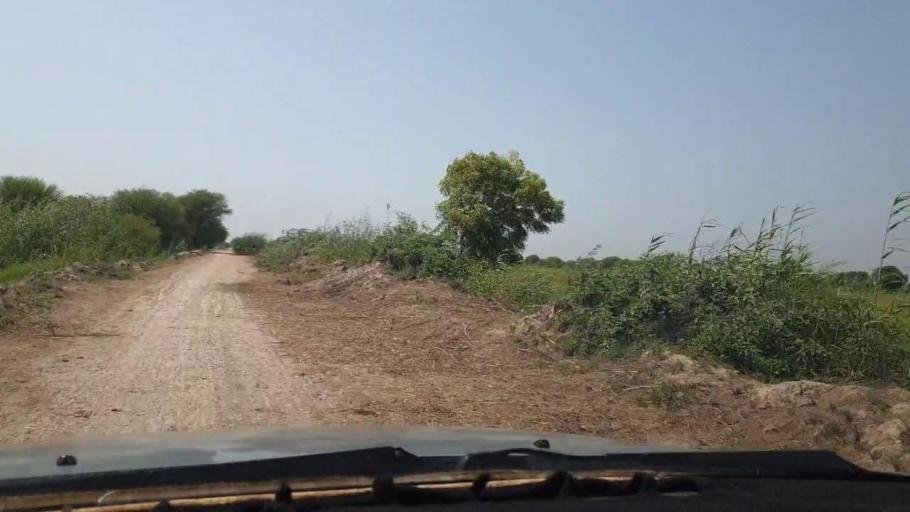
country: PK
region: Sindh
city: Tando Ghulam Ali
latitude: 25.1432
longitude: 68.7990
